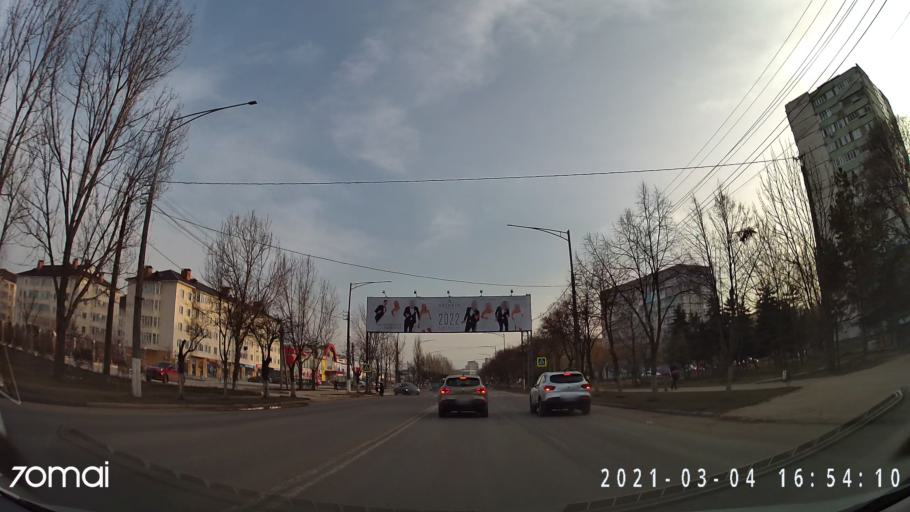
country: MD
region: Balti
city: Balti
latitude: 47.7653
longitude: 27.9415
